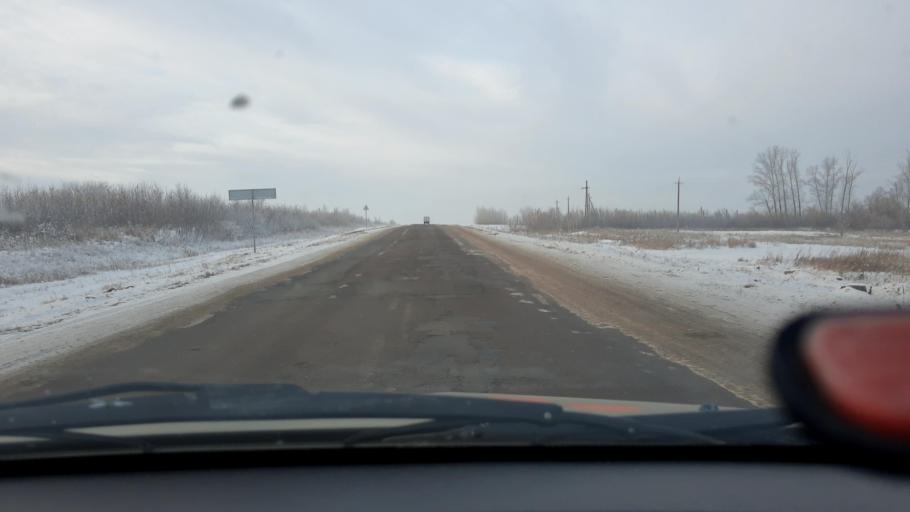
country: RU
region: Bashkortostan
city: Avdon
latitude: 54.3652
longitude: 55.8288
